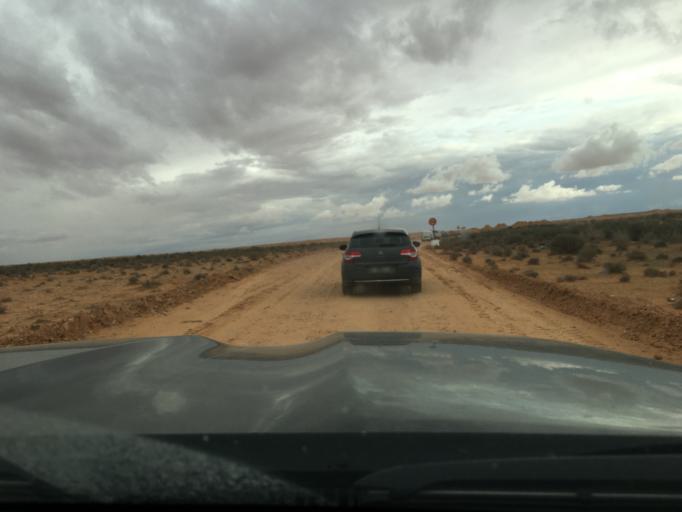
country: TN
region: Madanin
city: Medenine
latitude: 33.2611
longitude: 10.5729
